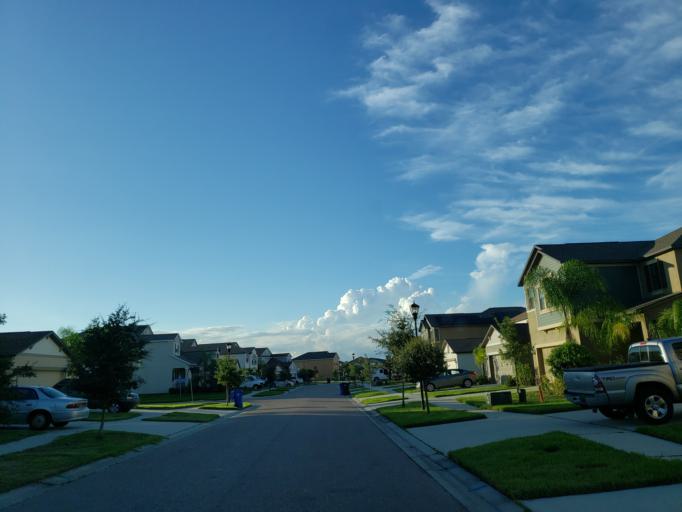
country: US
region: Florida
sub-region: Hillsborough County
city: Ruskin
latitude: 27.7293
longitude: -82.4082
